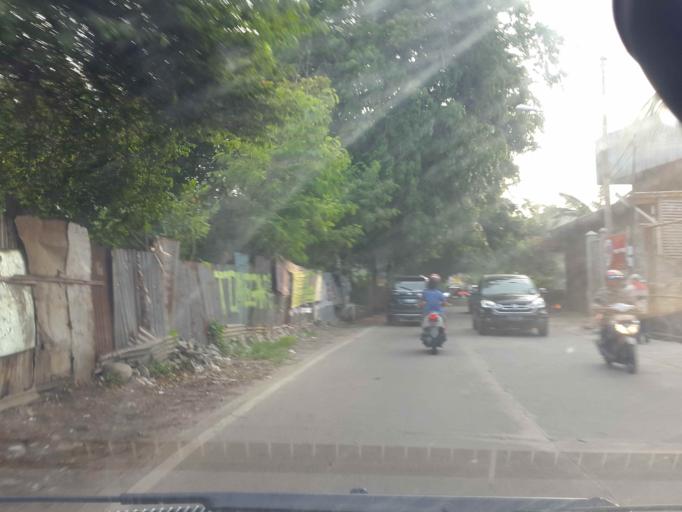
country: ID
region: Banten
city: South Tangerang
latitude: -6.2661
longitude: 106.7444
